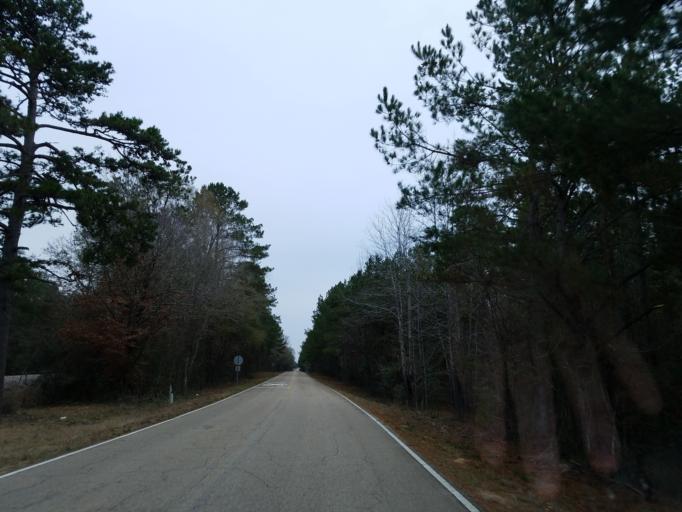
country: US
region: Mississippi
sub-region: Forrest County
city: Hattiesburg
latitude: 31.2551
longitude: -89.2335
